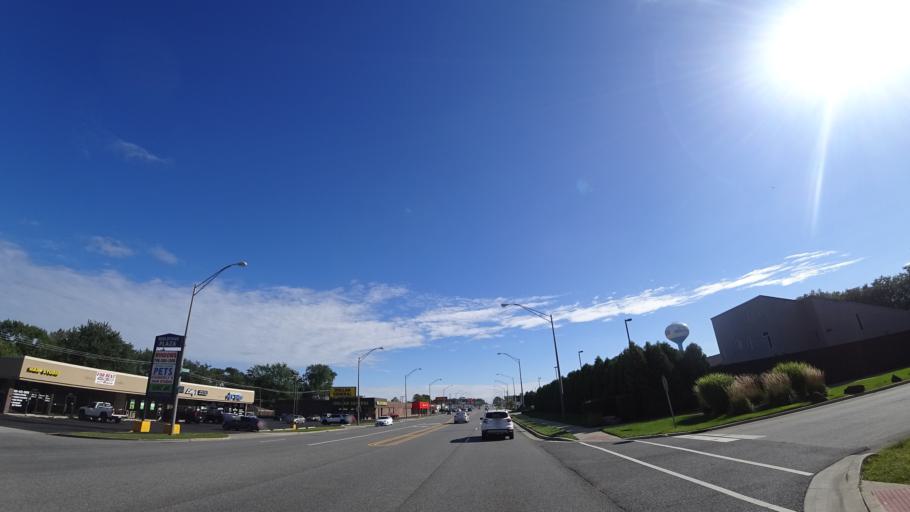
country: US
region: Illinois
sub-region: Cook County
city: Midlothian
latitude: 41.6310
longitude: -87.7376
